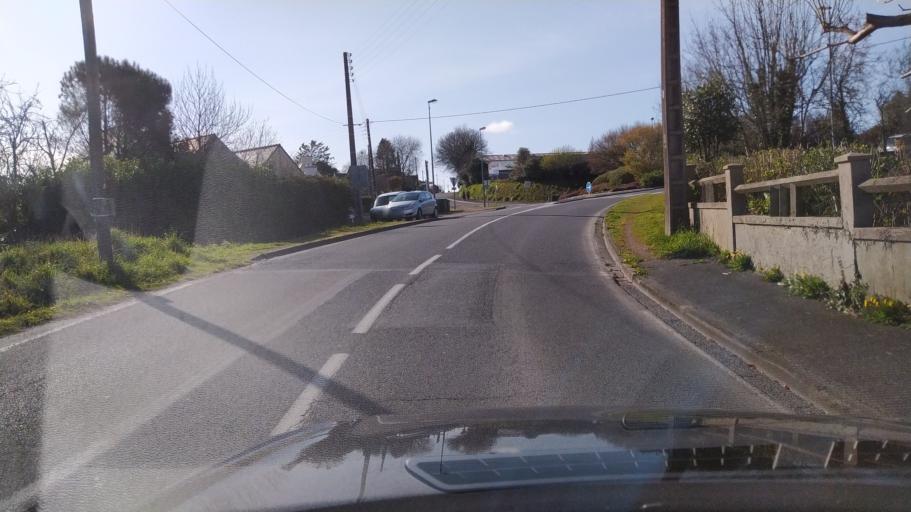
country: FR
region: Brittany
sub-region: Departement du Finistere
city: Landivisiau
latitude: 48.5010
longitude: -4.0696
